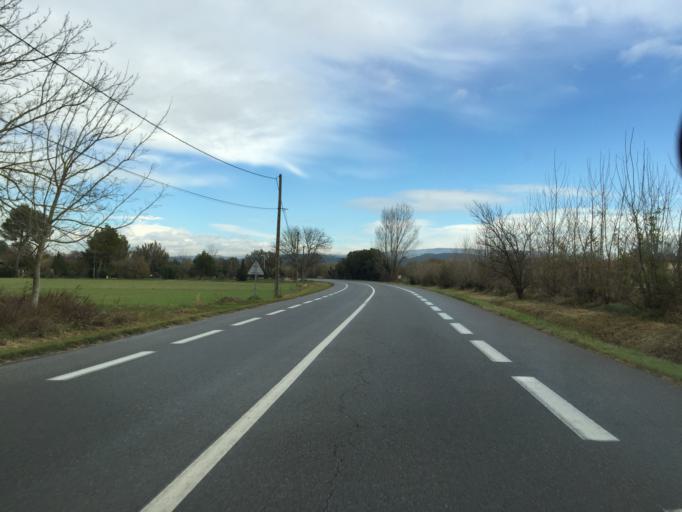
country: FR
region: Provence-Alpes-Cote d'Azur
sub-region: Departement du Vaucluse
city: Velleron
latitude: 43.9801
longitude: 5.0108
